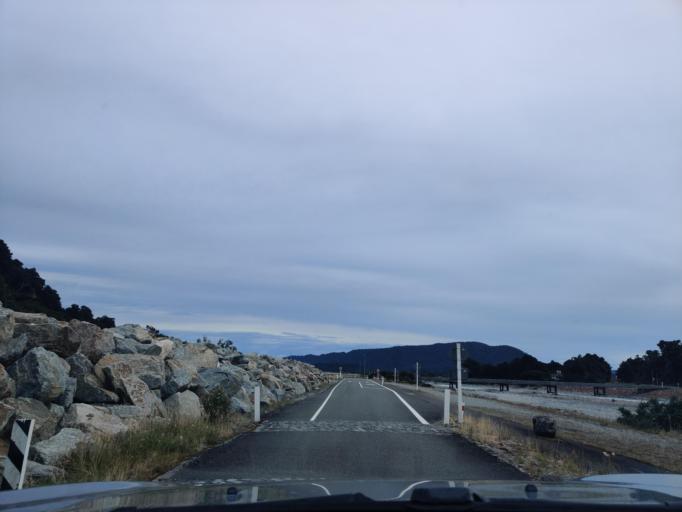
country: NZ
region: West Coast
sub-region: Westland District
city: Hokitika
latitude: -43.3959
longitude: 170.1810
